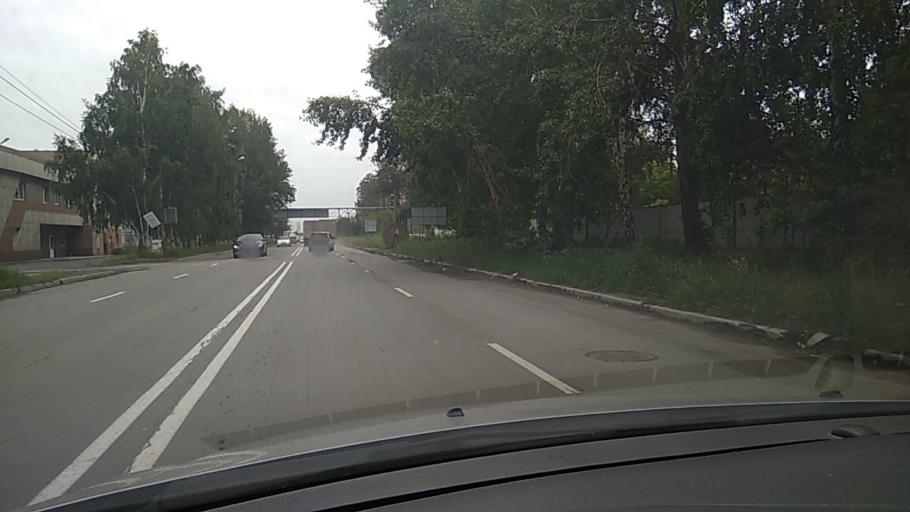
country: RU
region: Sverdlovsk
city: Shuvakish
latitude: 56.8896
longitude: 60.5221
